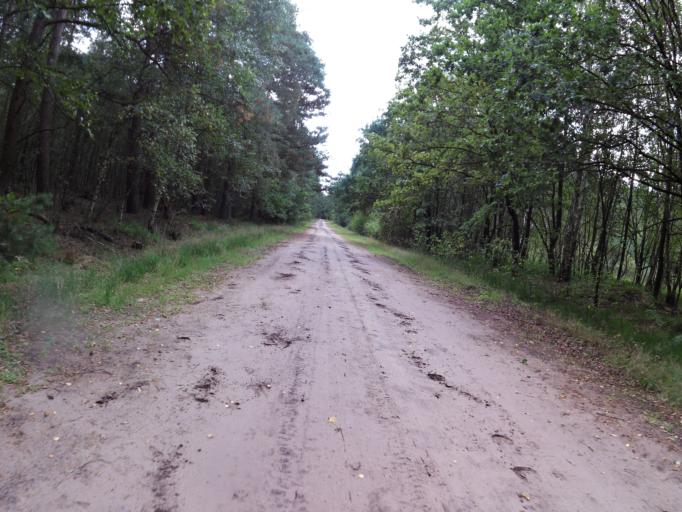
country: DE
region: Lower Saxony
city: Sandbostel
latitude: 53.3715
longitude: 9.1518
